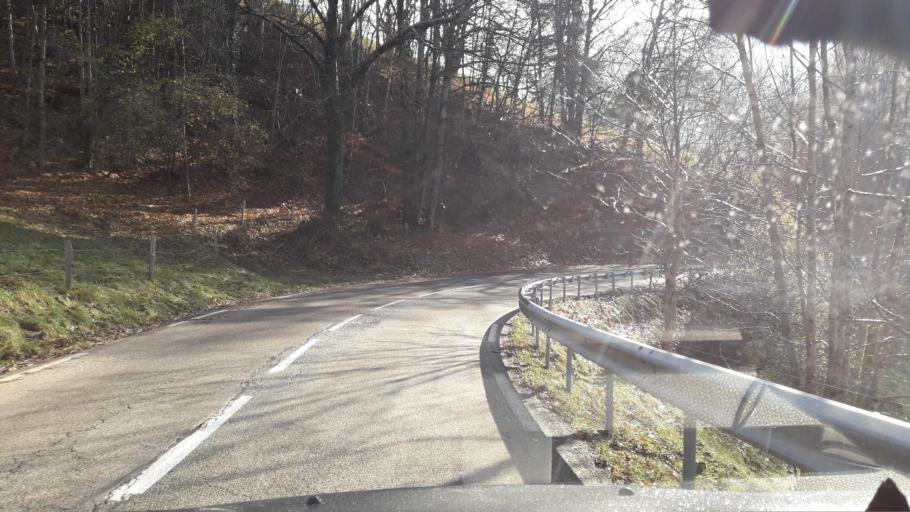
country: FR
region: Rhone-Alpes
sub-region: Departement de l'Isere
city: Allevard
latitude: 45.3943
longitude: 6.0829
